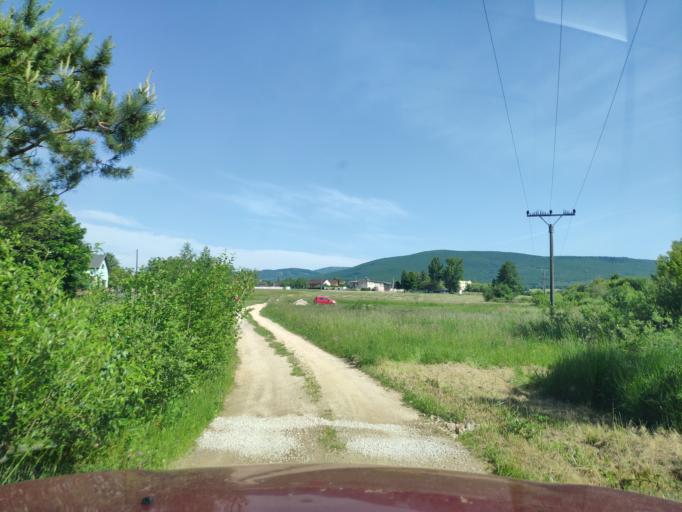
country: SK
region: Kosicky
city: Moldava nad Bodvou
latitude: 48.6904
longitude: 21.0123
